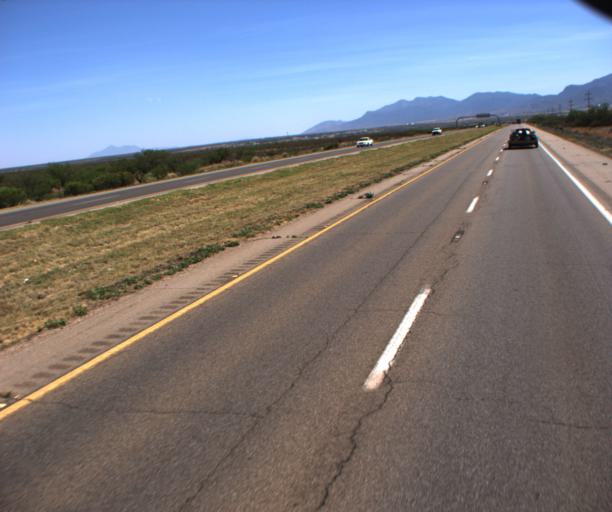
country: US
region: Arizona
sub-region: Cochise County
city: Huachuca City
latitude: 31.6743
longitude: -110.3504
